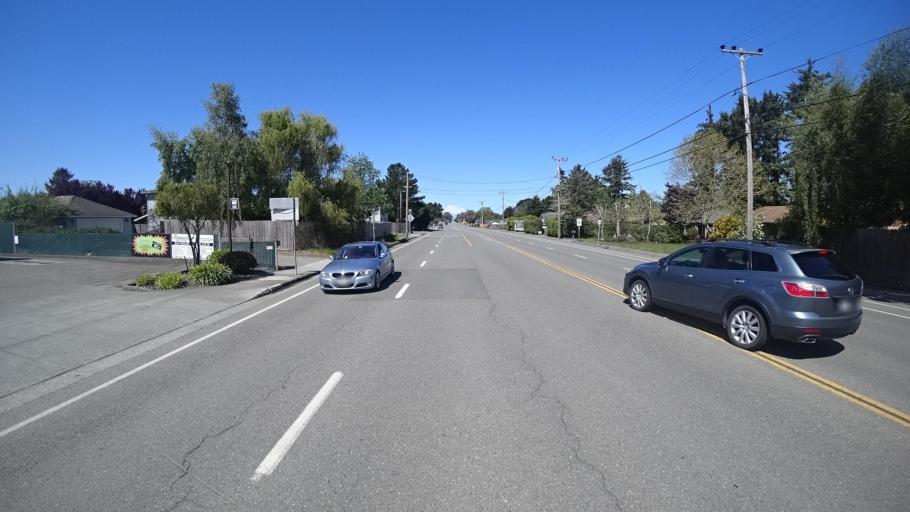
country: US
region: California
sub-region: Humboldt County
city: McKinleyville
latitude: 40.9562
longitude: -124.1016
